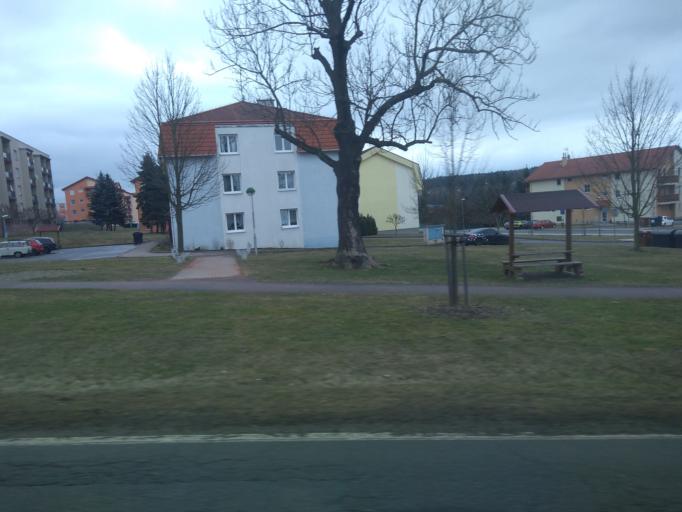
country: CZ
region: Plzensky
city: Vejprnice
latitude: 49.7309
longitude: 13.2779
